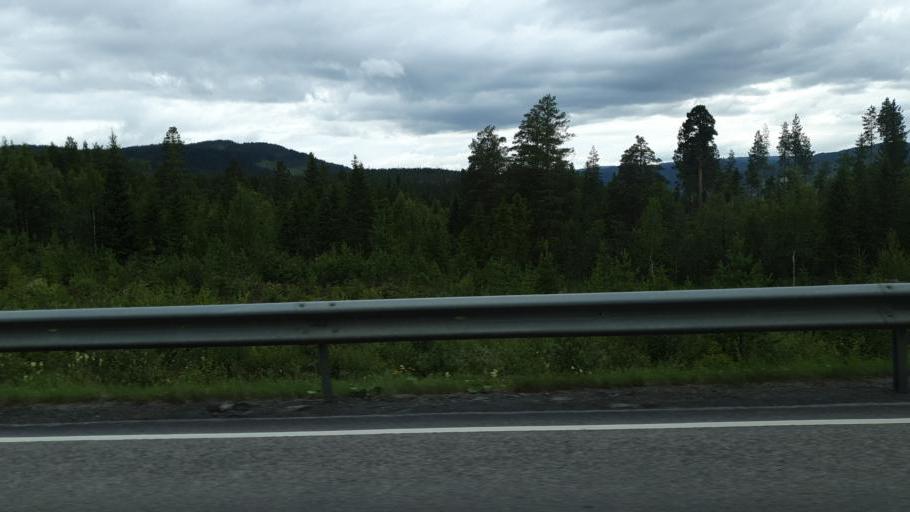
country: NO
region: Sor-Trondelag
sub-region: Rennebu
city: Berkak
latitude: 62.7967
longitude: 10.0218
